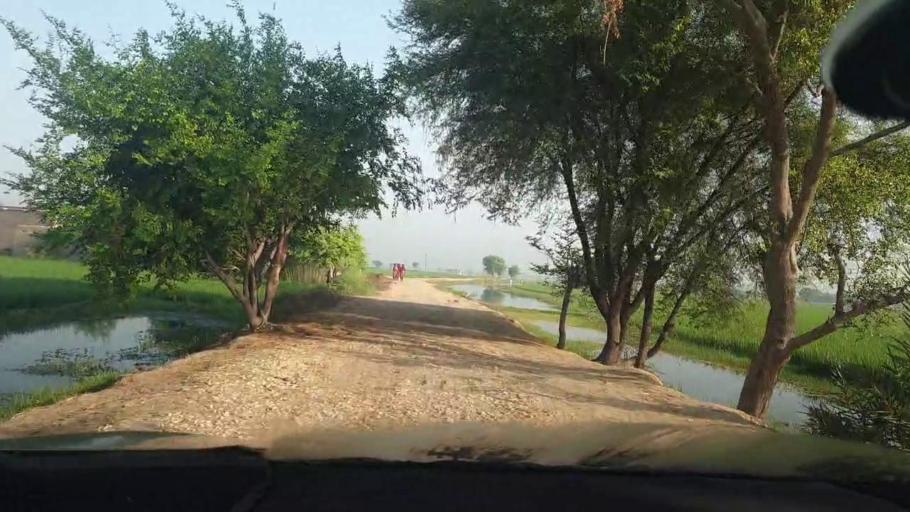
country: PK
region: Sindh
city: Kambar
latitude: 27.6297
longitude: 68.0176
